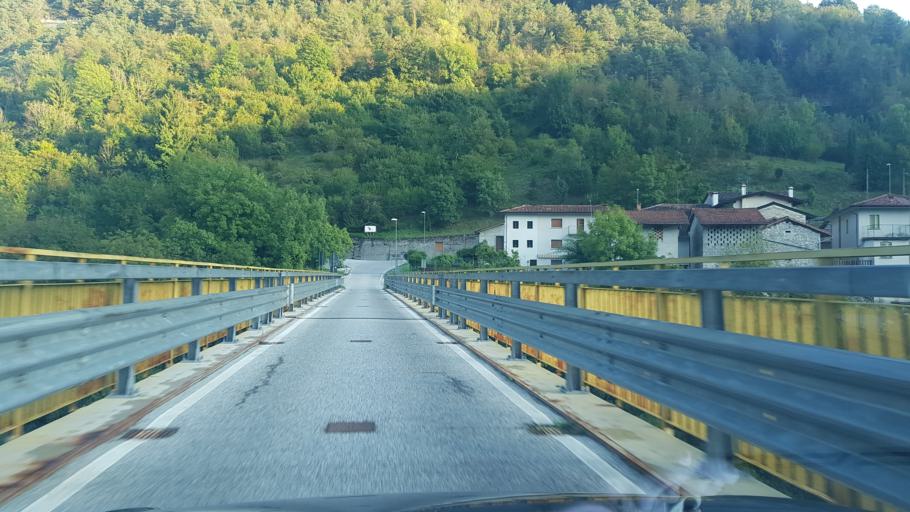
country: IT
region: Friuli Venezia Giulia
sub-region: Provincia di Pordenone
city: Frisanco
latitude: 46.2538
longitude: 12.7363
